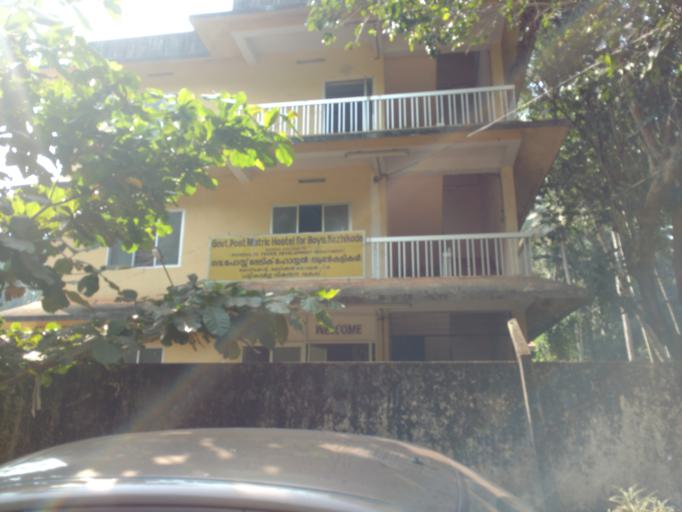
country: IN
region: Kerala
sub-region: Kozhikode
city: Kunnamangalam
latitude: 11.3016
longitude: 75.8236
